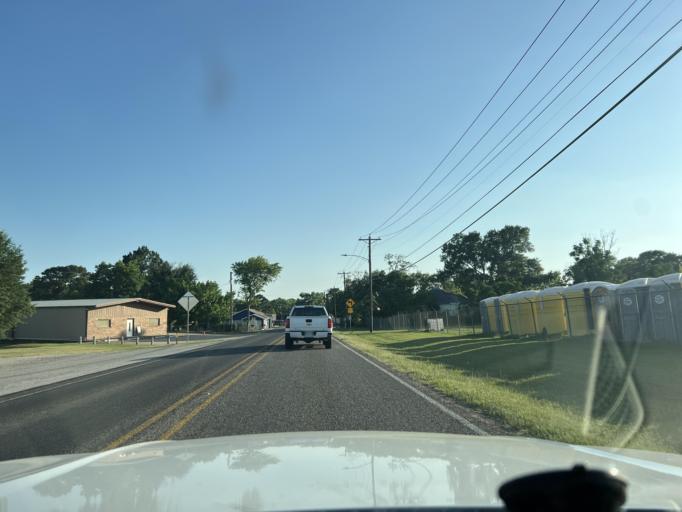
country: US
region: Texas
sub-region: Washington County
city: Brenham
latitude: 30.1745
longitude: -96.3889
